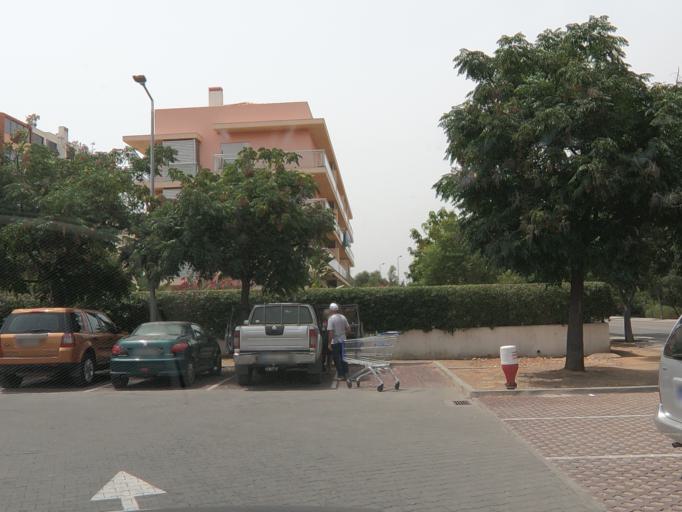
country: PT
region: Faro
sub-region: Portimao
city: Portimao
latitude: 37.1345
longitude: -8.5478
